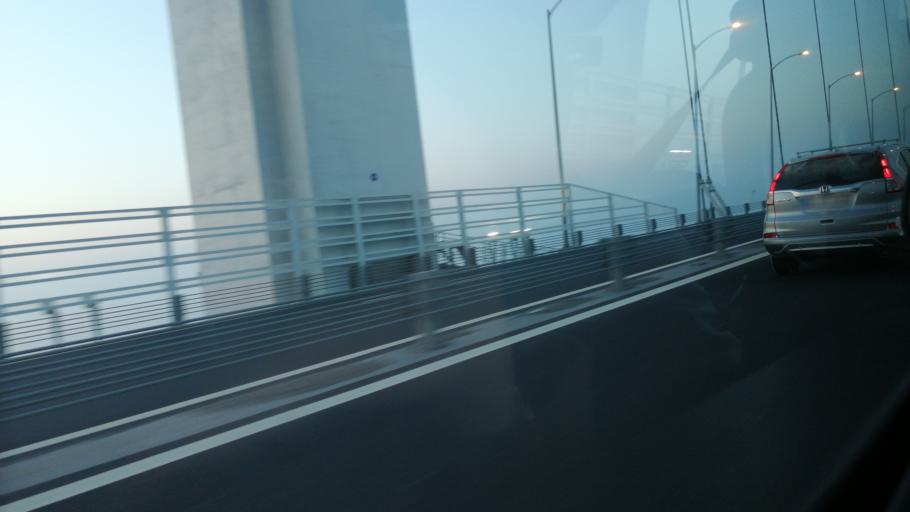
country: TR
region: Kocaeli
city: Tavsancil
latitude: 40.7616
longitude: 29.5170
